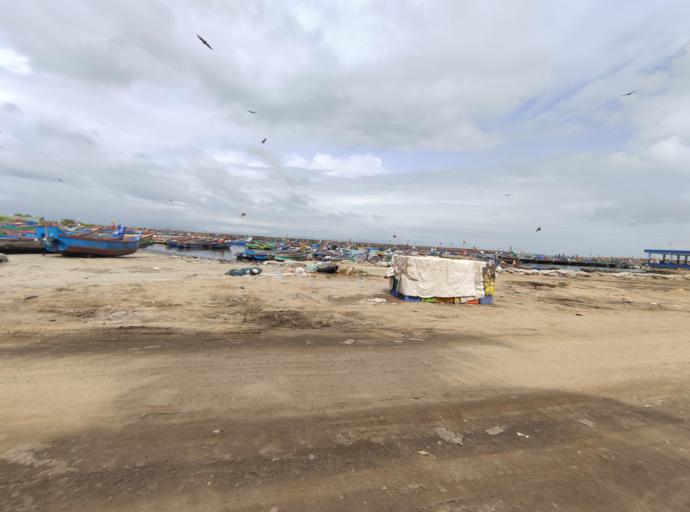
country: IN
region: Kerala
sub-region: Alappuzha
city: Kutiatodu
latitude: 9.7995
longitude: 76.2758
